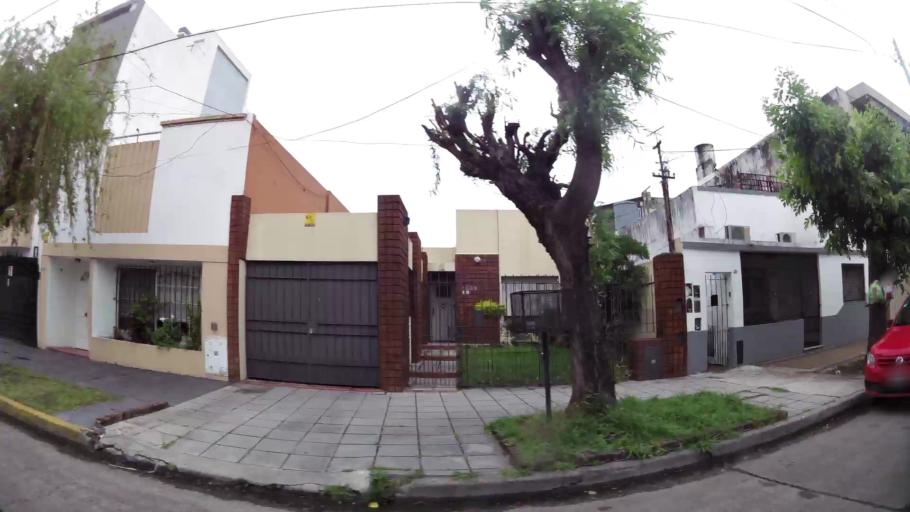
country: AR
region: Buenos Aires
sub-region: Partido de Lanus
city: Lanus
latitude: -34.7043
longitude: -58.3768
